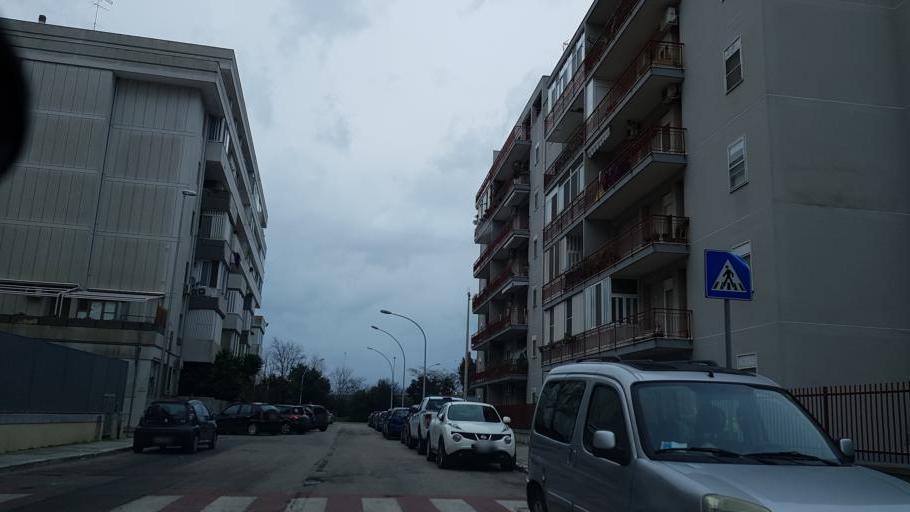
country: IT
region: Apulia
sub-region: Provincia di Brindisi
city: Brindisi
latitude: 40.6257
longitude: 17.9226
